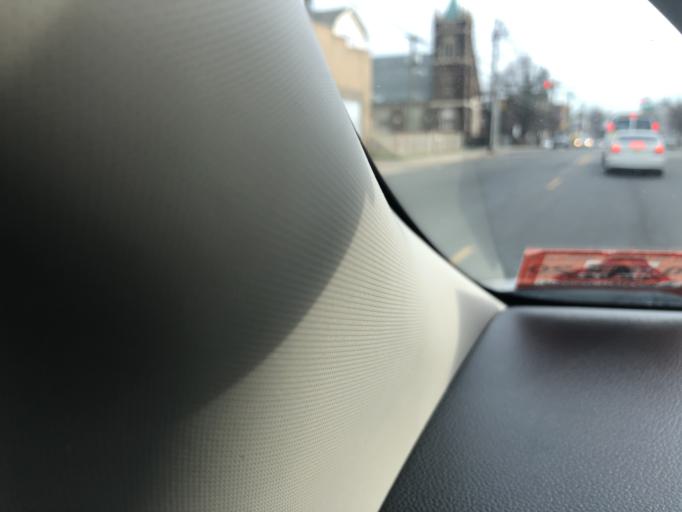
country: US
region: New Jersey
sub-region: Essex County
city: Irvington
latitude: 40.7276
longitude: -74.2099
